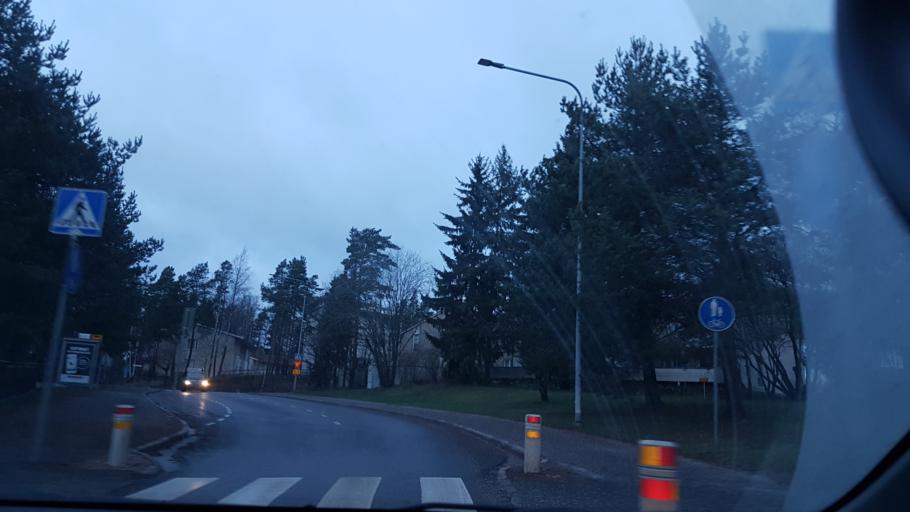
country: FI
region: Uusimaa
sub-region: Helsinki
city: Vantaa
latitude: 60.2814
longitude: 25.1215
